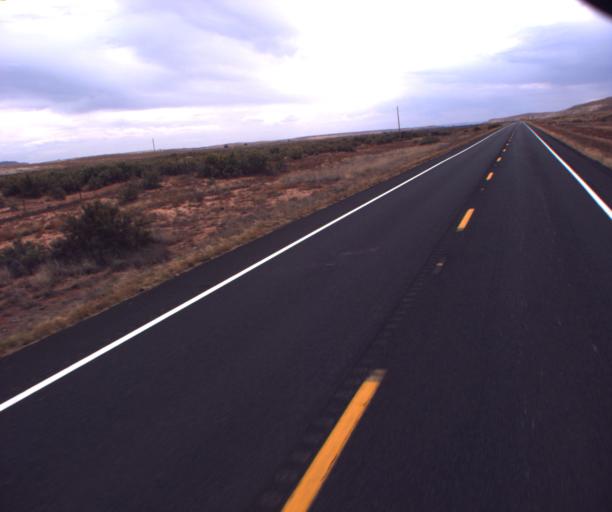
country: US
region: Arizona
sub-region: Coconino County
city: Kaibito
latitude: 36.3522
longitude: -110.9090
